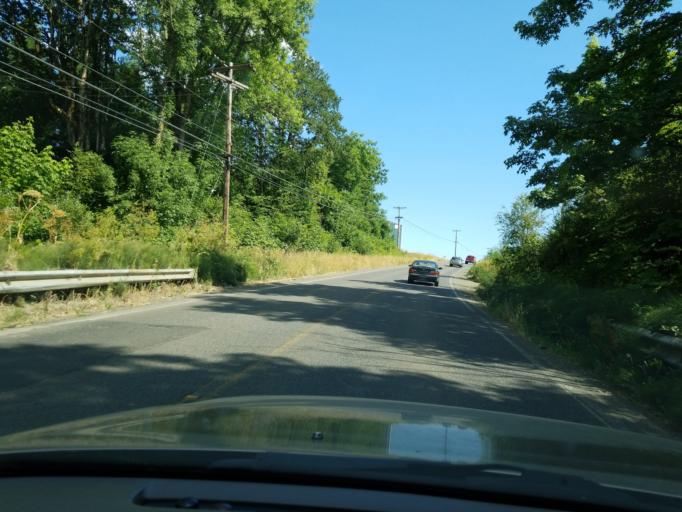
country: US
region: Oregon
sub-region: Yamhill County
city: McMinnville
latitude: 45.2533
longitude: -123.2014
